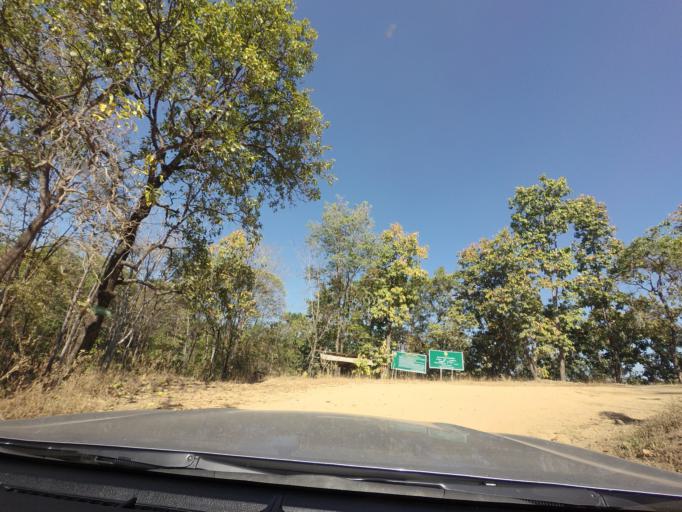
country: TH
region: Lampang
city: Chae Hom
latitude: 18.6151
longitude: 99.6531
